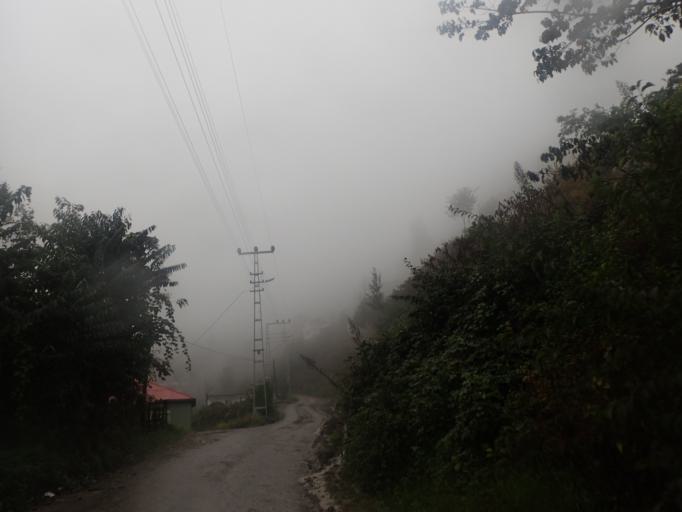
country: TR
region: Ordu
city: Persembe
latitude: 41.0399
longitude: 37.7235
